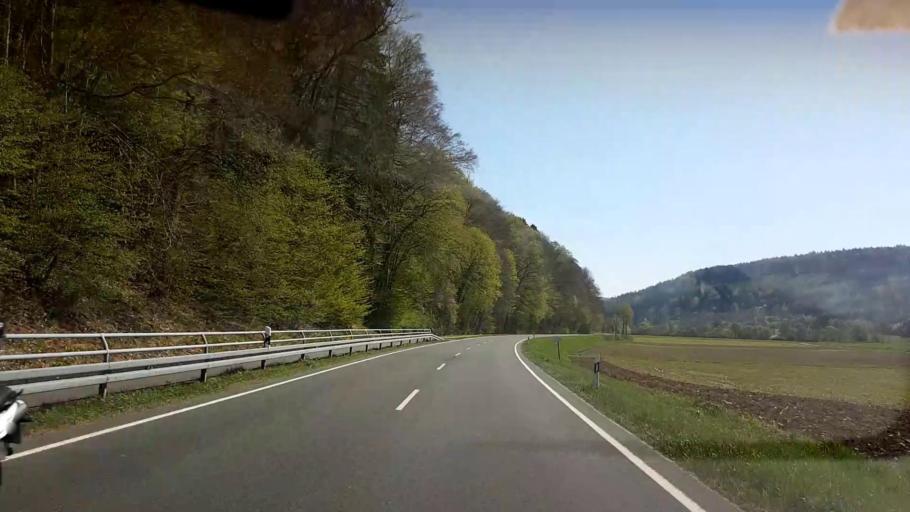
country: DE
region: Bavaria
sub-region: Upper Franconia
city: Unterleinleiter
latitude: 49.8134
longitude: 11.1947
